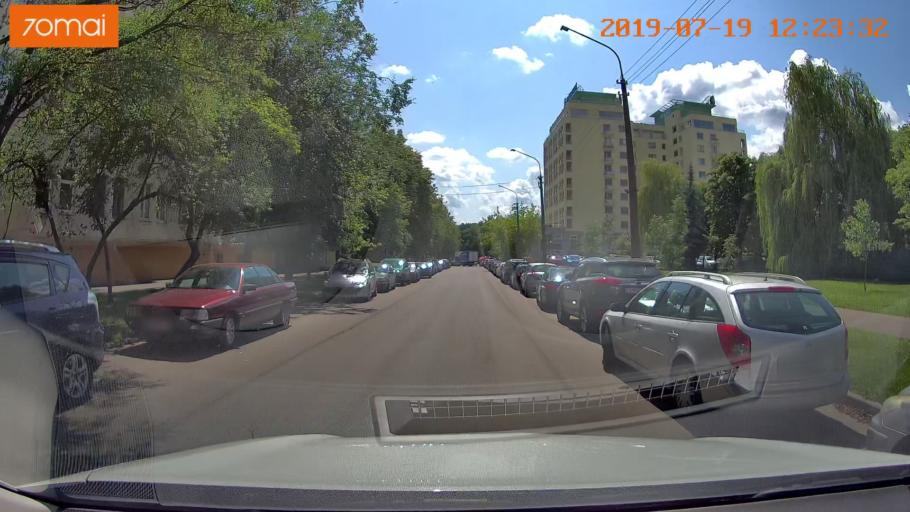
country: BY
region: Minsk
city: Minsk
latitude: 53.9274
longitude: 27.6184
